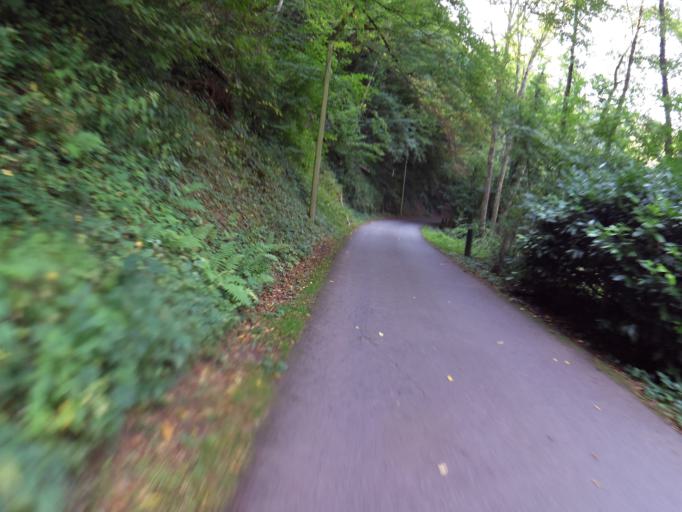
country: DE
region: Rheinland-Pfalz
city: Speicher
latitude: 49.9378
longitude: 6.6279
